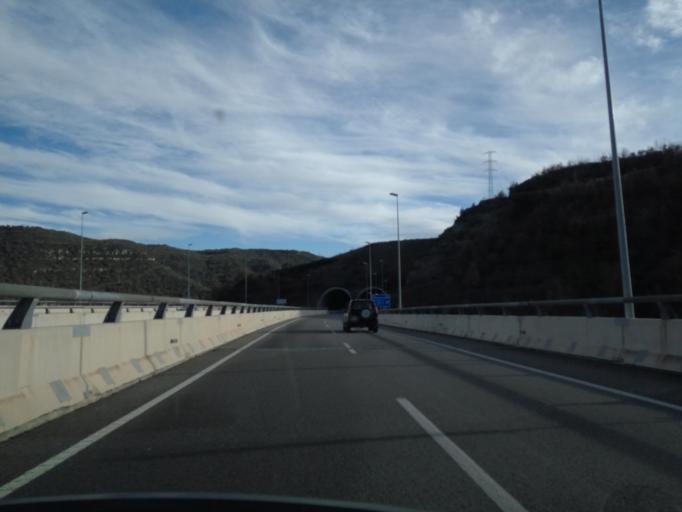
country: ES
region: Catalonia
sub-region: Provincia de Barcelona
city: Puig-reig
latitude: 41.9941
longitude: 1.8835
